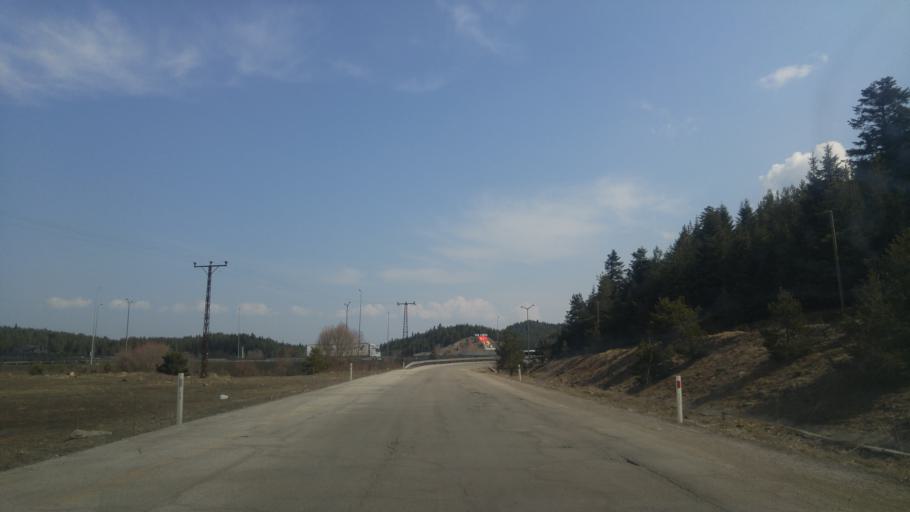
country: TR
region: Bolu
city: Gerede
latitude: 40.6104
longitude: 32.2548
